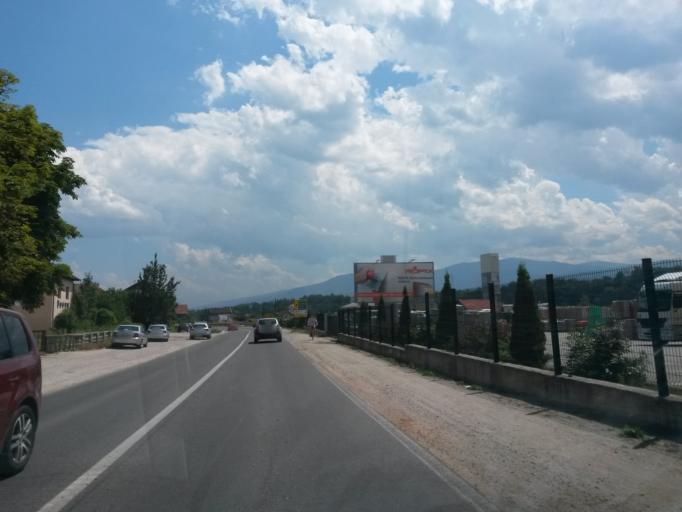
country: BA
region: Federation of Bosnia and Herzegovina
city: Vitez
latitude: 44.1733
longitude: 17.7581
